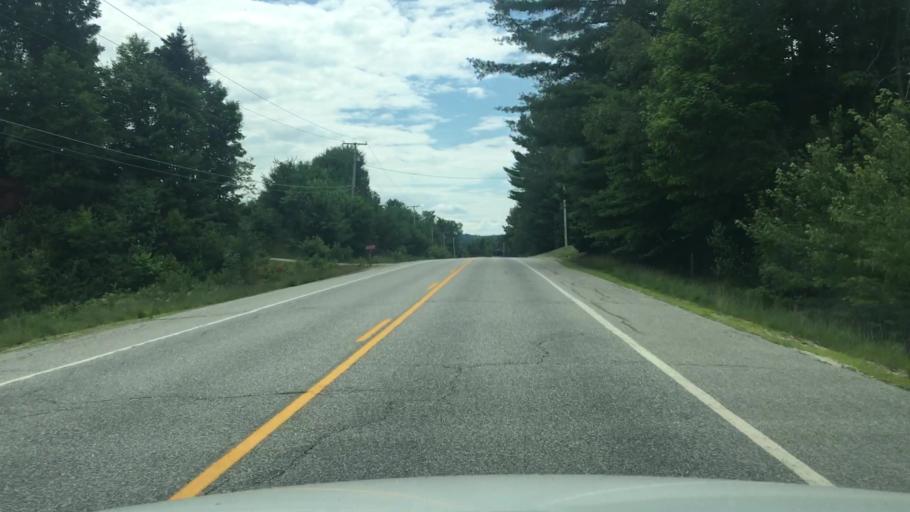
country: US
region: Maine
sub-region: Oxford County
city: West Paris
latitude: 44.3349
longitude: -70.5412
